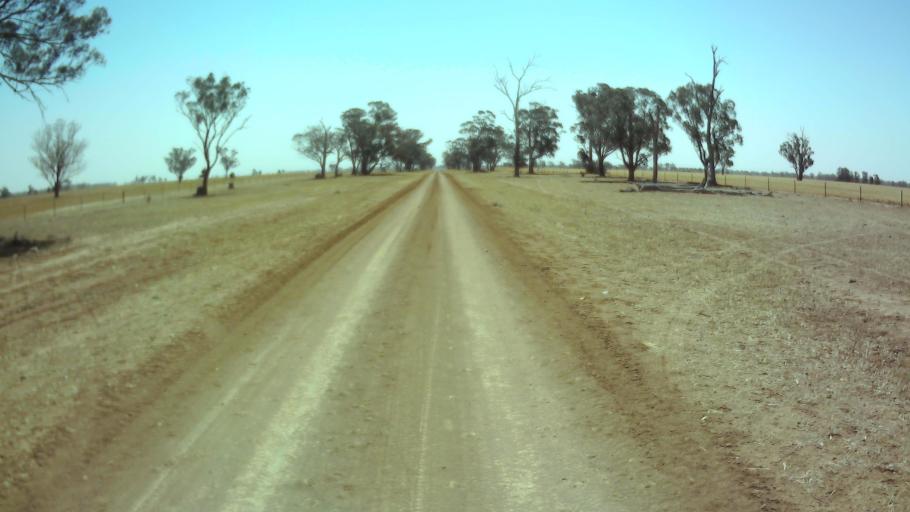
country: AU
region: New South Wales
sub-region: Weddin
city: Grenfell
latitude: -34.0090
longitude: 147.8887
